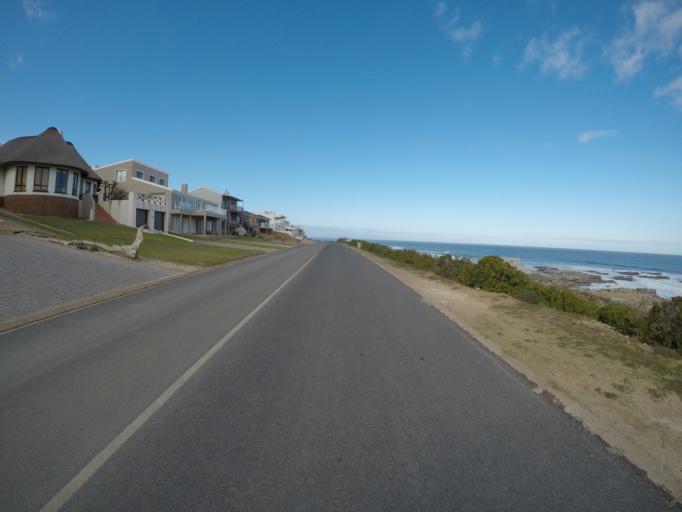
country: ZA
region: Western Cape
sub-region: Eden District Municipality
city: Riversdale
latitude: -34.4328
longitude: 21.3308
